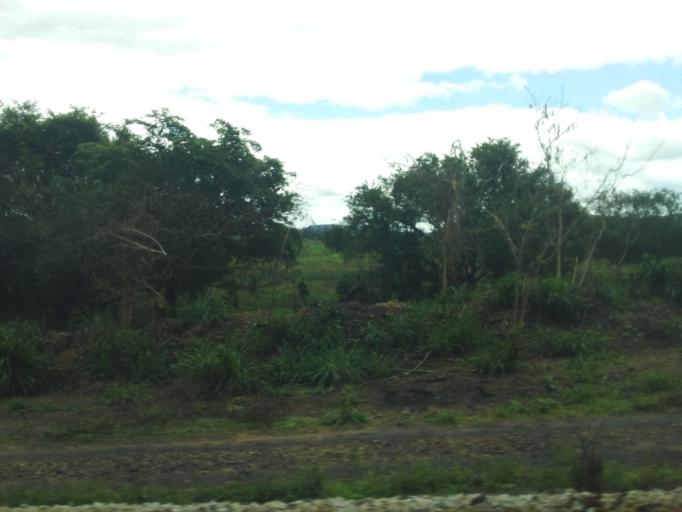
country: BR
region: Minas Gerais
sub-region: Governador Valadares
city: Governador Valadares
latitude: -19.0604
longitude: -42.1481
